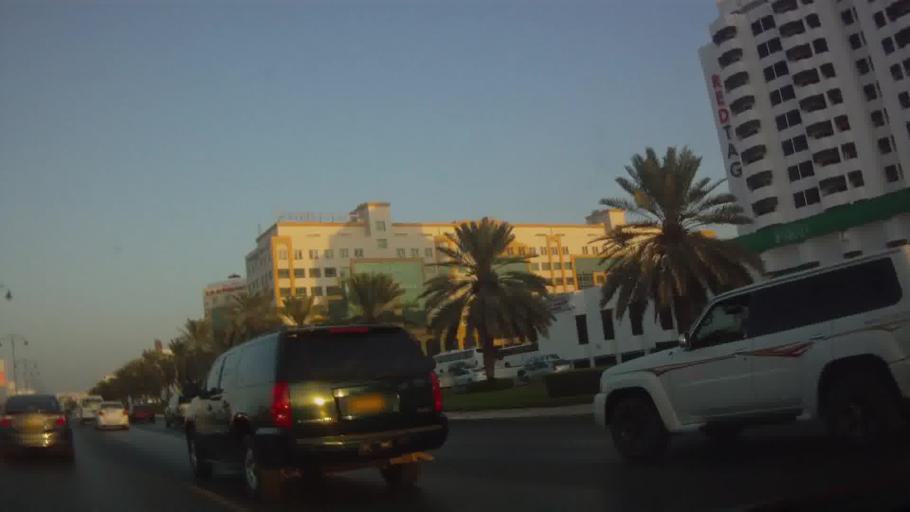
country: OM
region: Muhafazat Masqat
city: Bawshar
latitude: 23.5971
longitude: 58.4230
